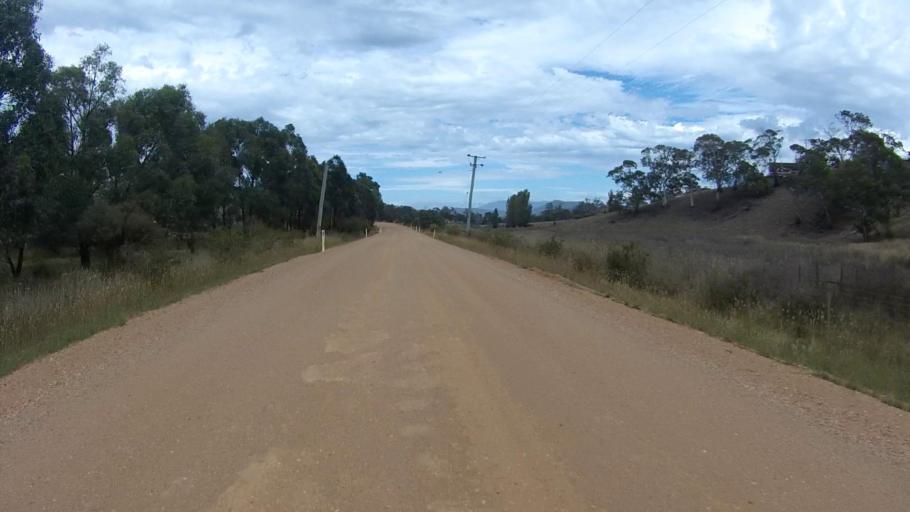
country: AU
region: Tasmania
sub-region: Sorell
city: Sorell
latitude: -42.6939
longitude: 147.4644
